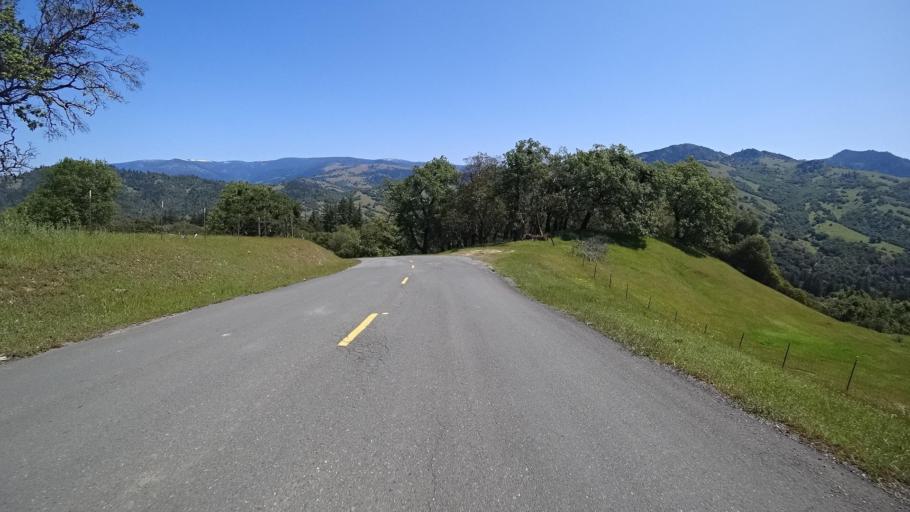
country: US
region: California
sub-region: Humboldt County
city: Redway
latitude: 40.1653
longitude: -123.6119
